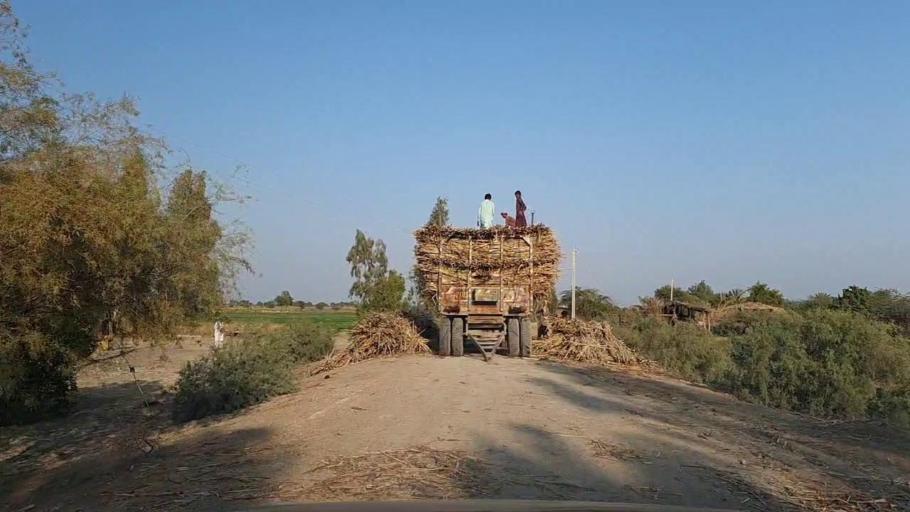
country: PK
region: Sindh
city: Tando Mittha Khan
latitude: 25.9278
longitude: 69.0959
